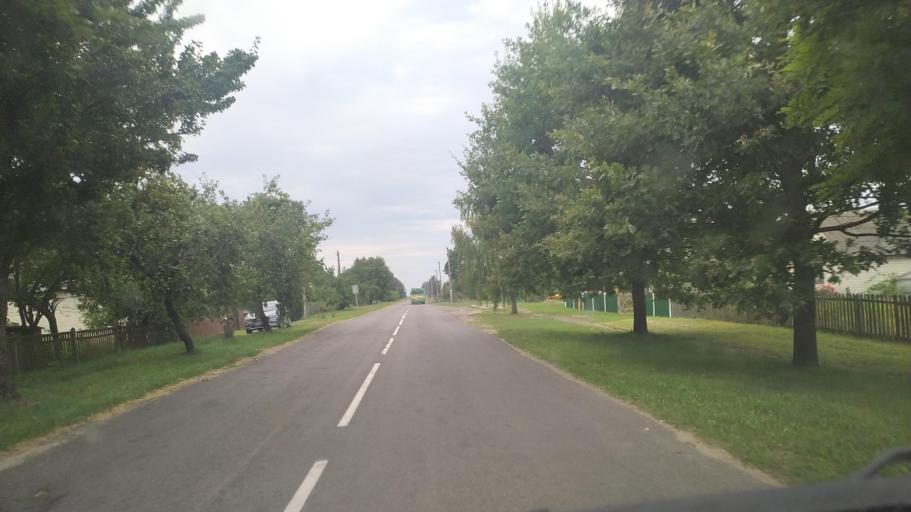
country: BY
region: Brest
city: Byaroza
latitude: 52.5826
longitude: 24.8616
